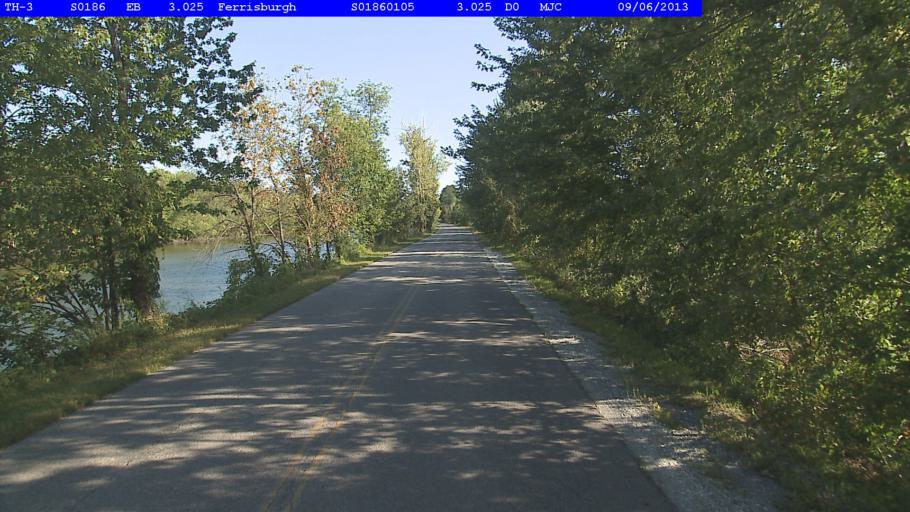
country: US
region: Vermont
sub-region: Addison County
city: Vergennes
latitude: 44.1829
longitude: -73.3097
